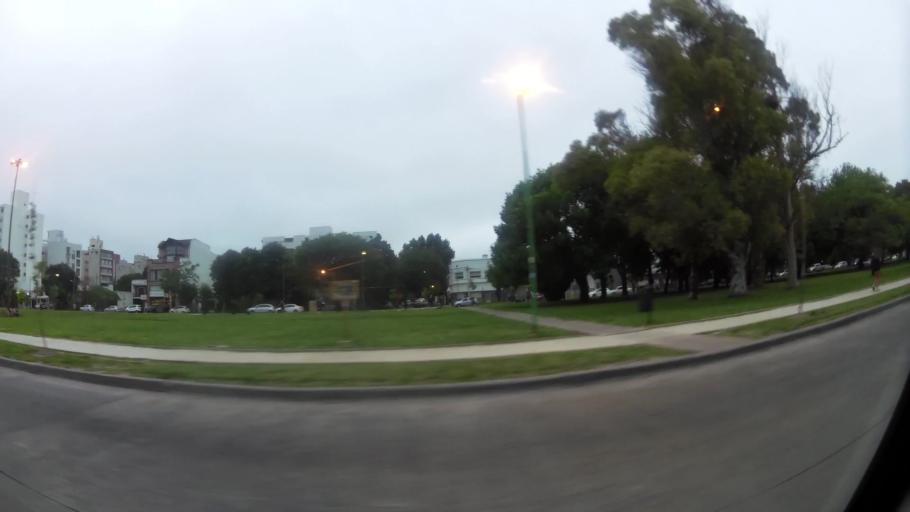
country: AR
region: Buenos Aires
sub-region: Partido de La Plata
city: La Plata
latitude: -34.9022
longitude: -57.9716
